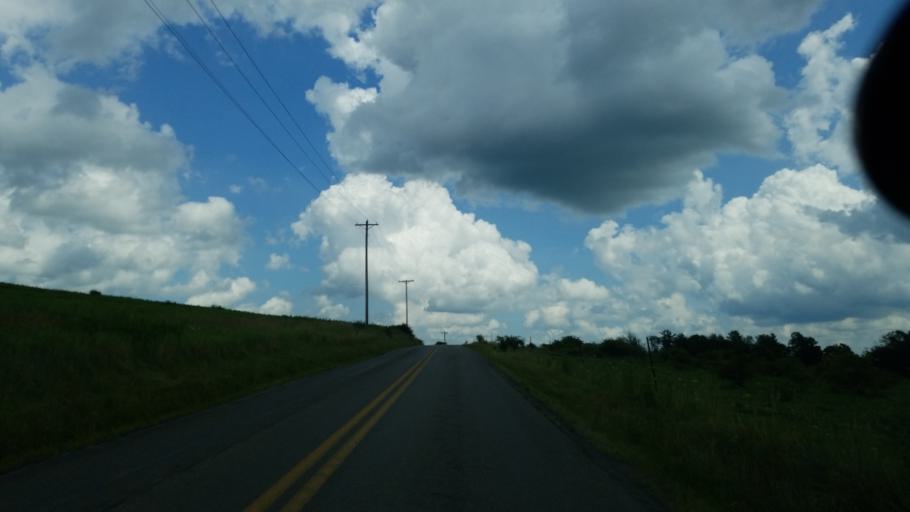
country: US
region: Pennsylvania
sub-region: Jefferson County
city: Brookville
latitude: 41.2329
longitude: -79.0761
